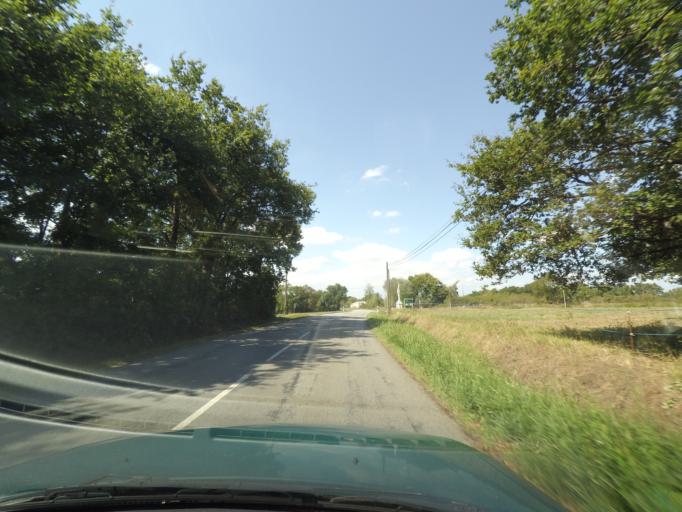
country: FR
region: Pays de la Loire
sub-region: Departement de la Loire-Atlantique
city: Sainte-Pazanne
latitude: 47.0738
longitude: -1.7807
